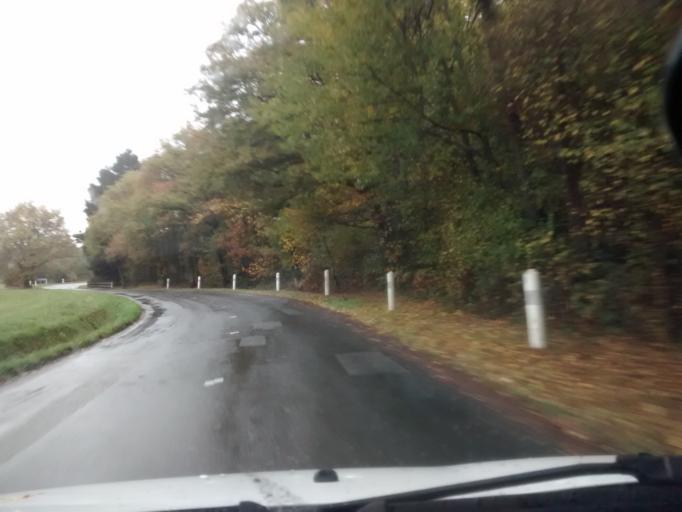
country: FR
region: Brittany
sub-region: Departement d'Ille-et-Vilaine
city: Chantepie
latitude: 48.0748
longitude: -1.6050
